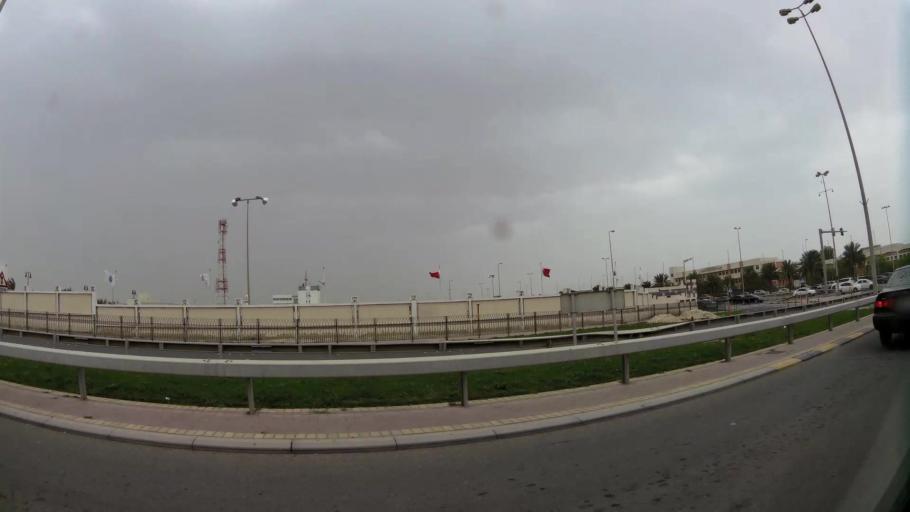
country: BH
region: Northern
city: Madinat `Isa
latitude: 26.1567
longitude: 50.5417
